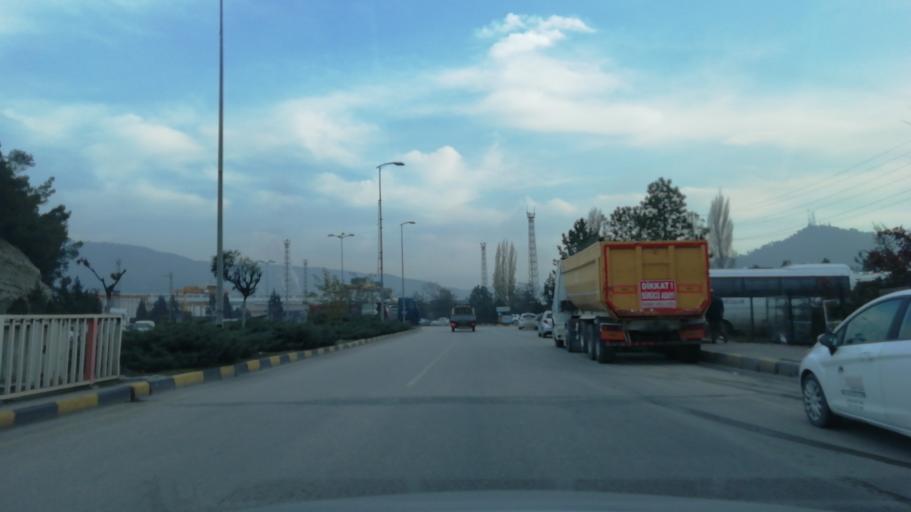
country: TR
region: Karabuk
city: Karabuk
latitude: 41.1949
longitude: 32.6240
